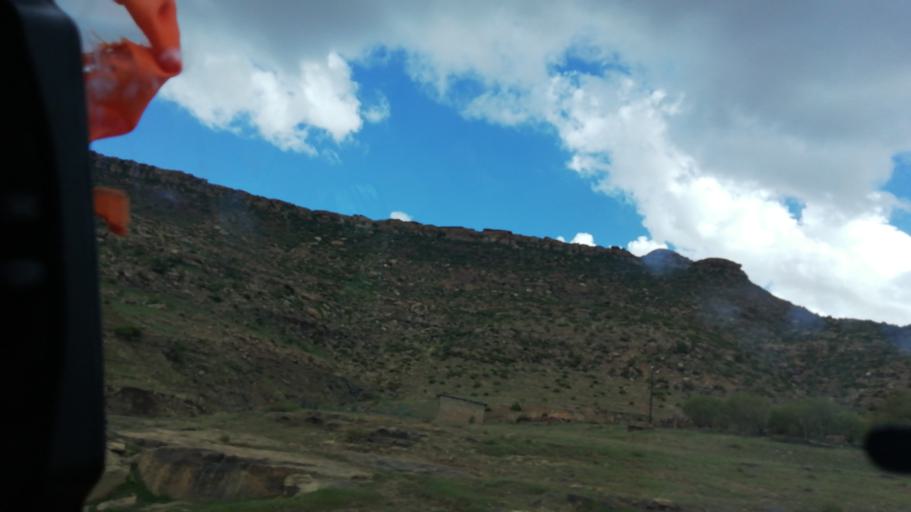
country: LS
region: Maseru
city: Maseru
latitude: -29.4435
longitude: 27.4206
